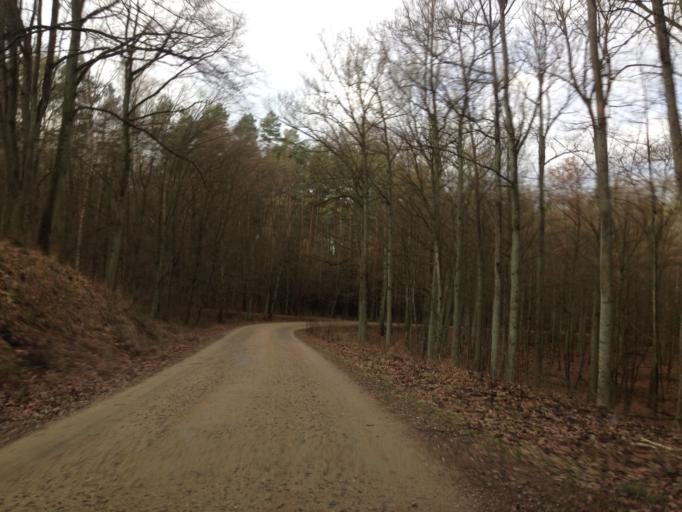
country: PL
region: Kujawsko-Pomorskie
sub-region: Powiat brodnicki
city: Gorzno
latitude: 53.2202
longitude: 19.6719
